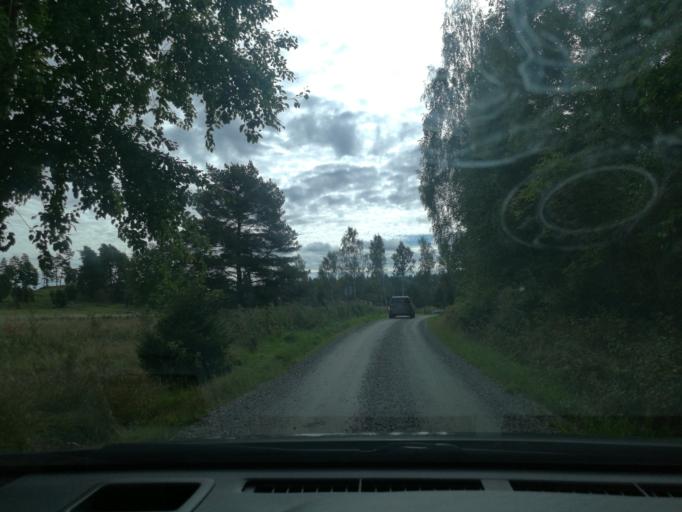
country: SE
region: OEstergoetland
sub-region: Soderkopings Kommun
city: Soederkoeping
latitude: 58.4849
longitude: 16.4728
